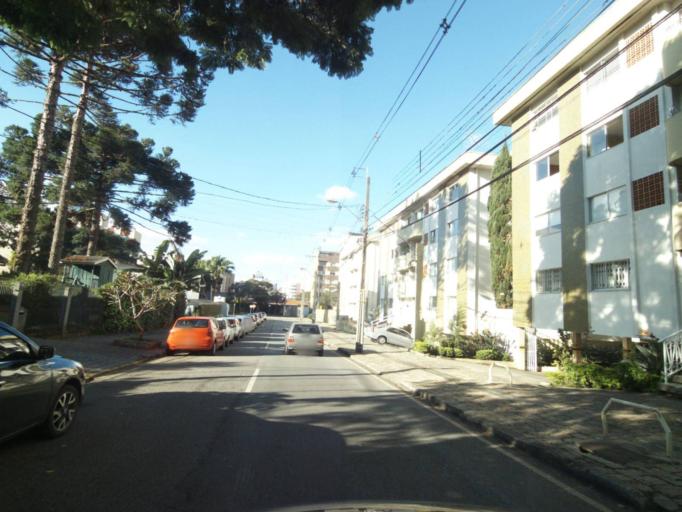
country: BR
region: Parana
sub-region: Curitiba
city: Curitiba
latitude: -25.4206
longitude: -49.2581
